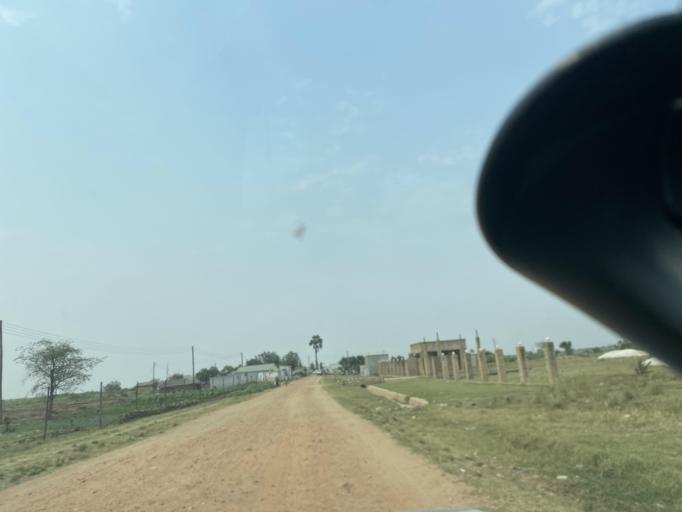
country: ZM
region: Lusaka
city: Kafue
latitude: -15.6874
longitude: 28.0075
